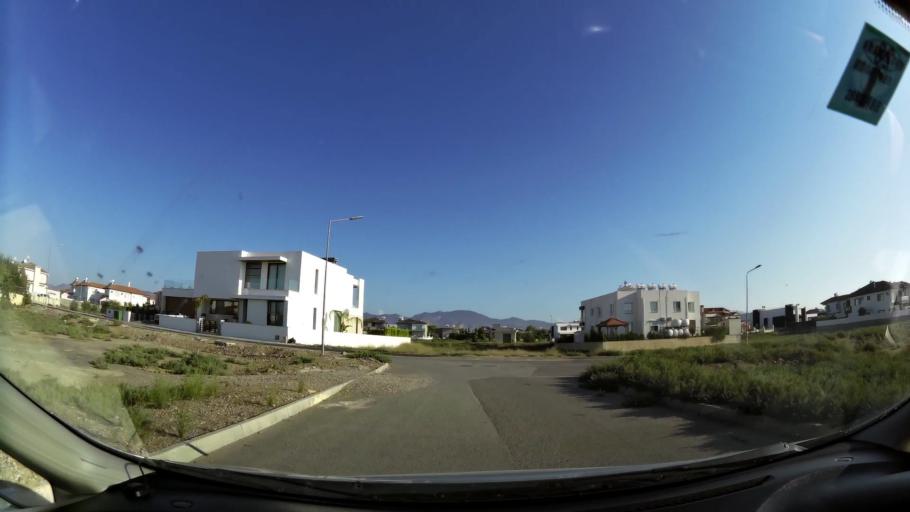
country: CY
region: Lefkosia
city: Nicosia
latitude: 35.2024
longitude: 33.3010
